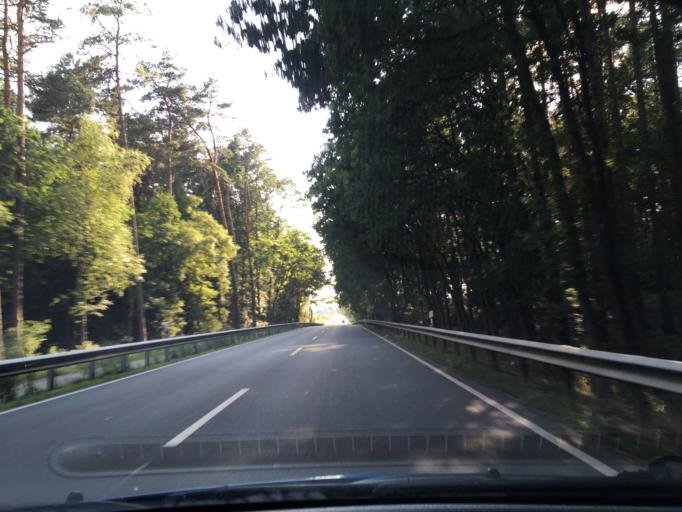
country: DE
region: Lower Saxony
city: Zernien
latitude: 53.0593
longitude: 10.8419
